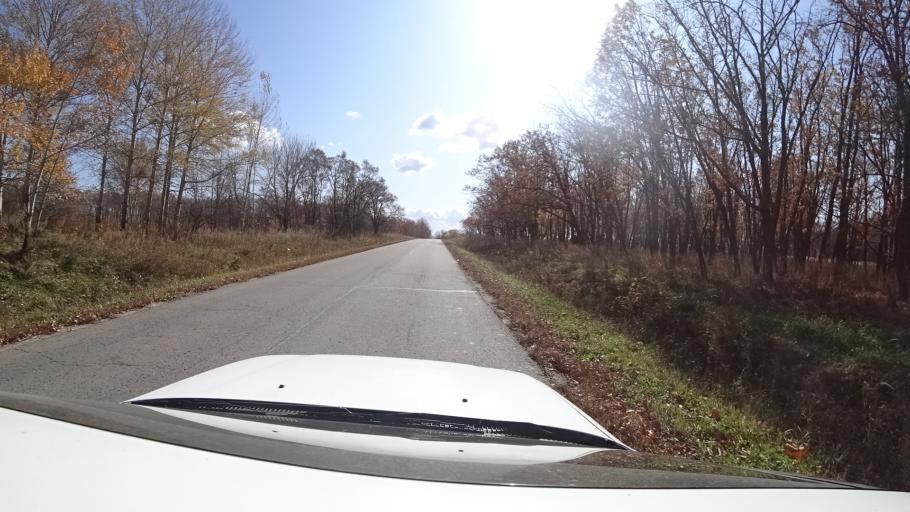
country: RU
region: Primorskiy
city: Lazo
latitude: 45.8697
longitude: 133.6608
